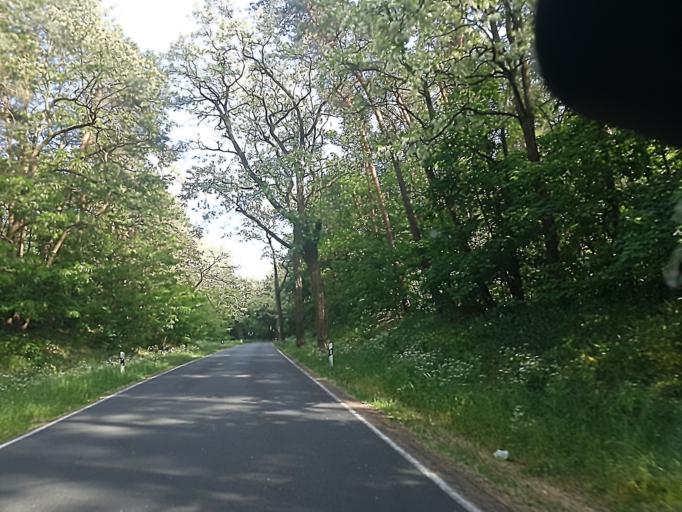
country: DE
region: Saxony-Anhalt
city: Kropstadt
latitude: 51.9839
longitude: 12.7020
